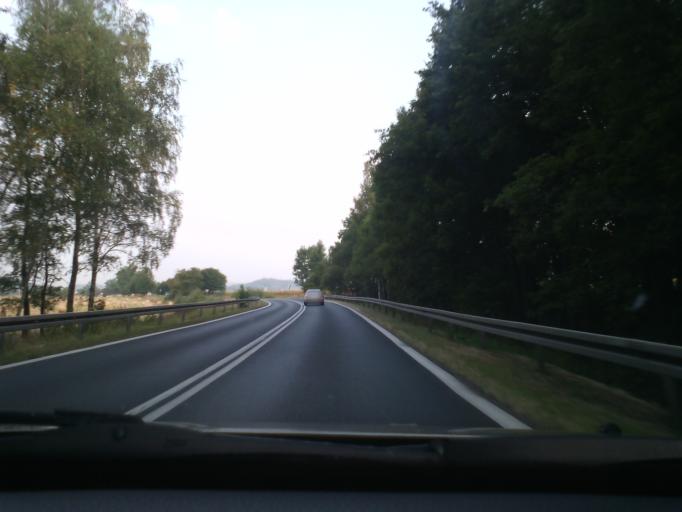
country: PL
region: Lower Silesian Voivodeship
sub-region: Powiat jeleniogorski
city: Janowice Wielkie
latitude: 50.9045
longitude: 15.8637
